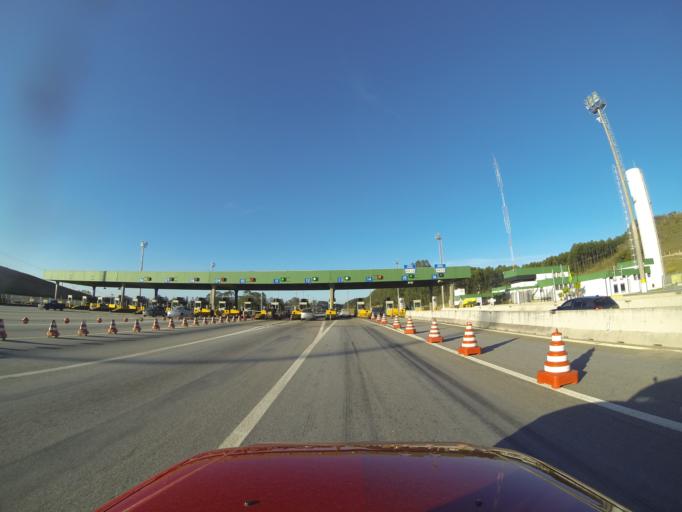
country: BR
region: Sao Paulo
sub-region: Jacarei
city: Jacarei
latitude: -23.2840
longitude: -45.8611
